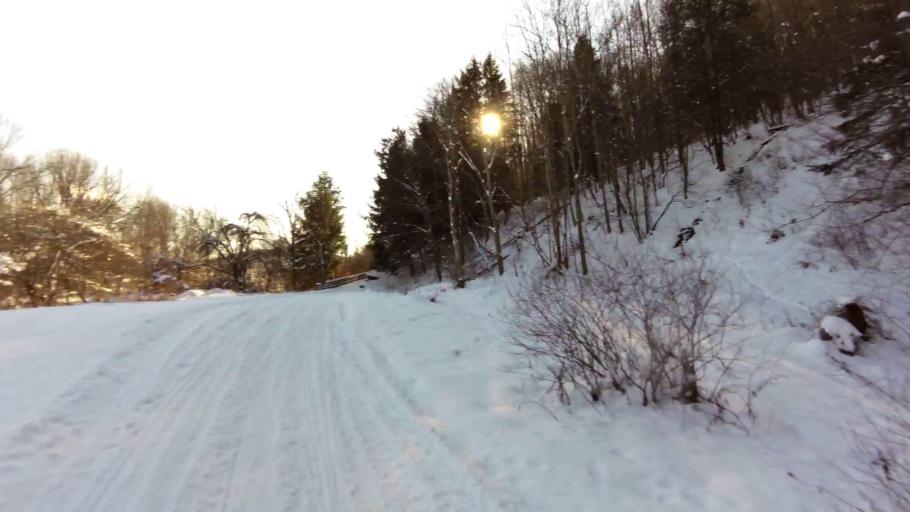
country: US
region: New York
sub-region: Cattaraugus County
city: Salamanca
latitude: 42.1051
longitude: -78.7517
